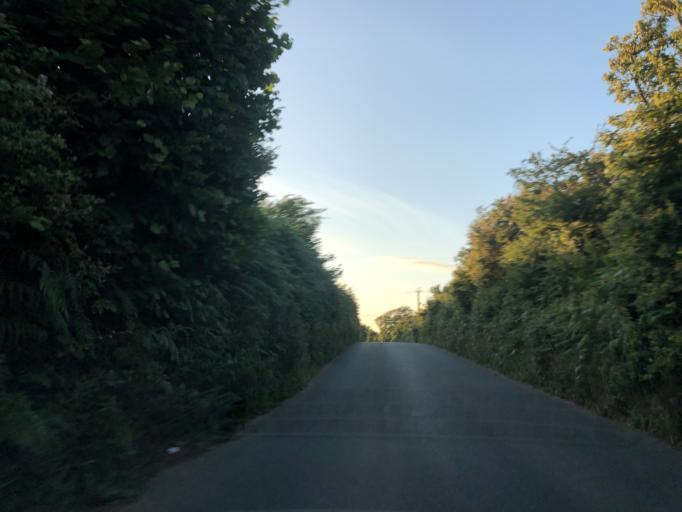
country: GB
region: England
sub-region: Isle of Wight
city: Newport
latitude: 50.6471
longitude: -1.2803
